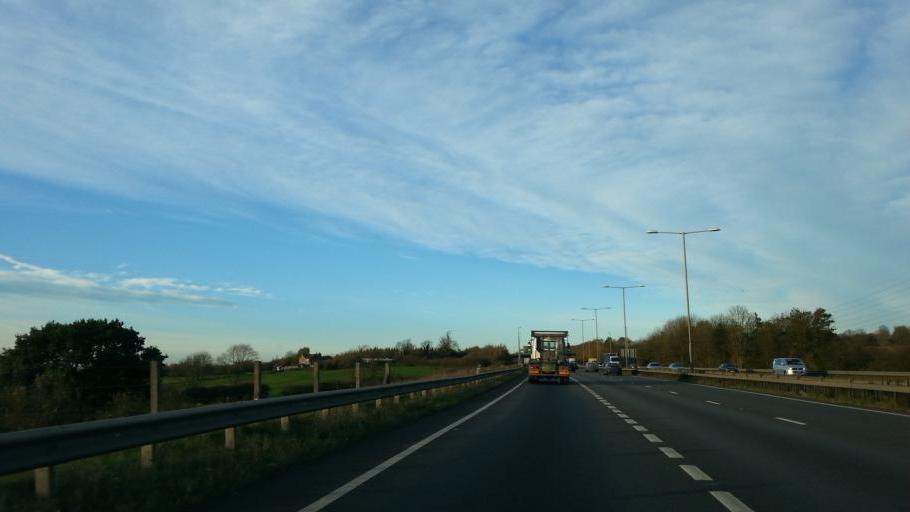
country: GB
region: England
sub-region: Northamptonshire
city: Kettering
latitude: 52.3984
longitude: -0.7503
